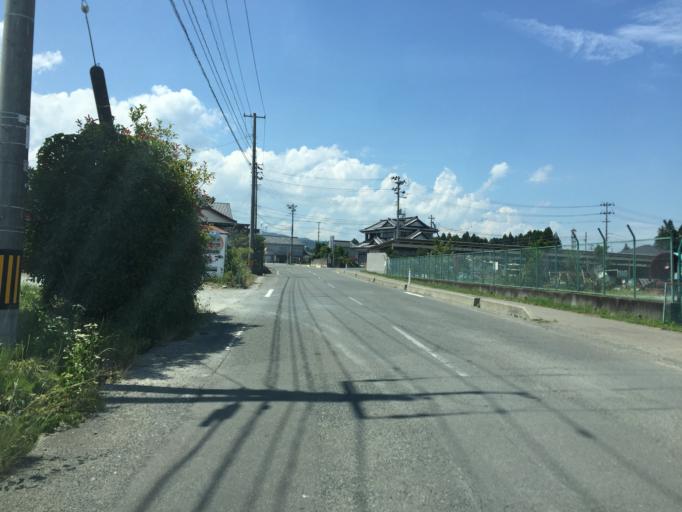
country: JP
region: Fukushima
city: Namie
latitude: 37.7192
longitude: 140.9312
